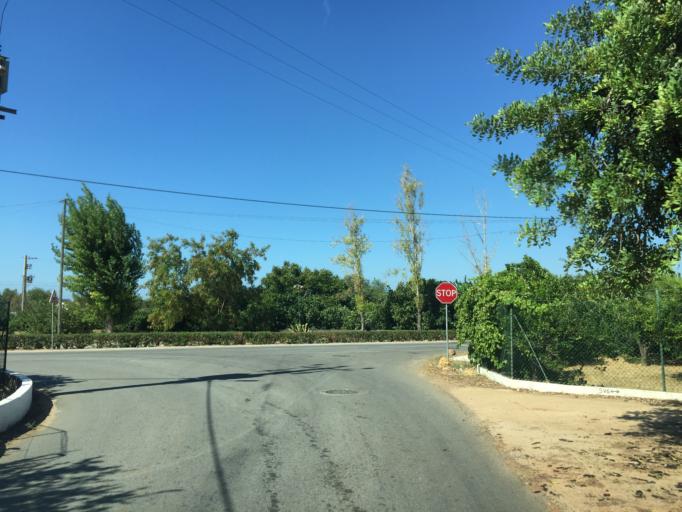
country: PT
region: Faro
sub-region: Loule
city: Vilamoura
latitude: 37.1117
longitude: -8.0885
